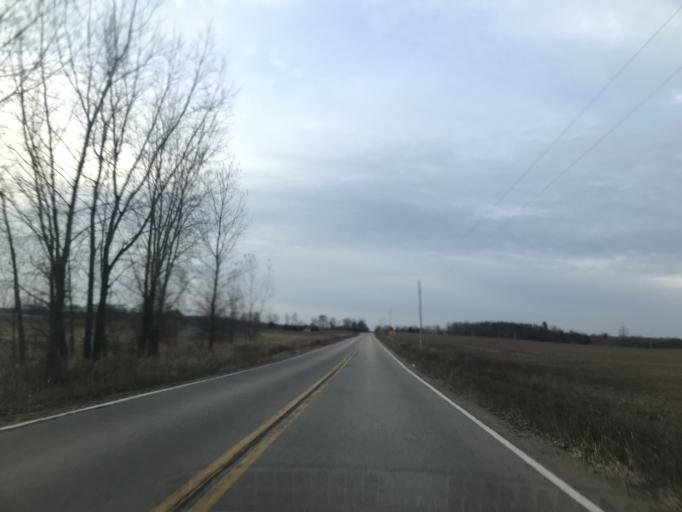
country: US
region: Wisconsin
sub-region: Marinette County
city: Peshtigo
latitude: 45.0976
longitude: -87.7993
